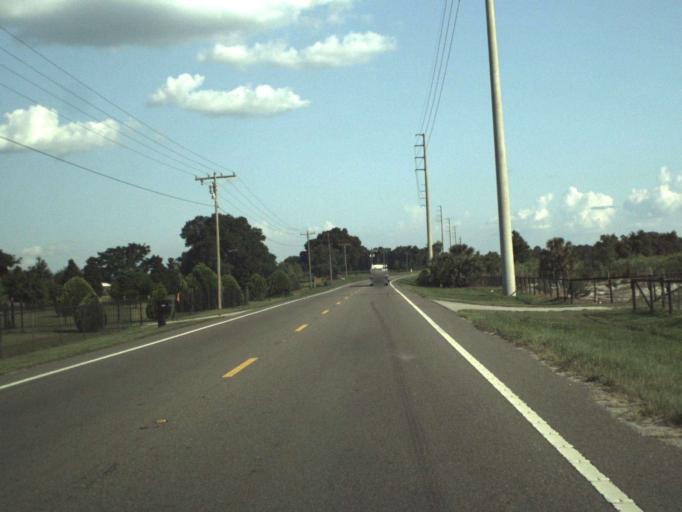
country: US
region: Florida
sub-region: Lake County
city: Groveland
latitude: 28.5271
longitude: -81.8469
